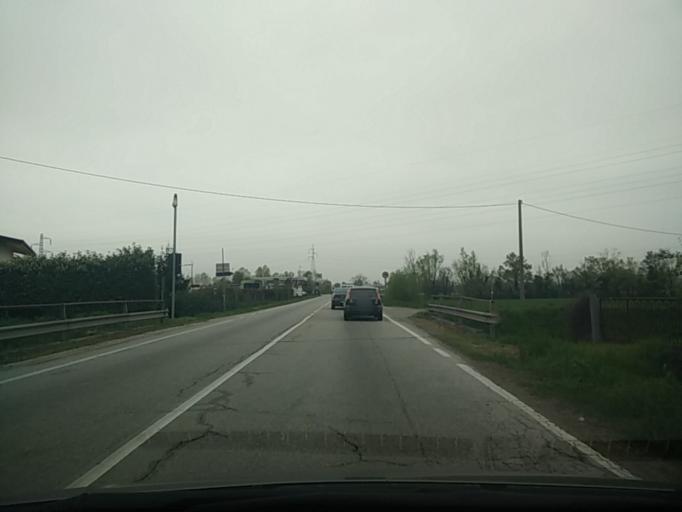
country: IT
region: Veneto
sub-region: Provincia di Venezia
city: Fornase
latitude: 45.4773
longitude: 12.1545
